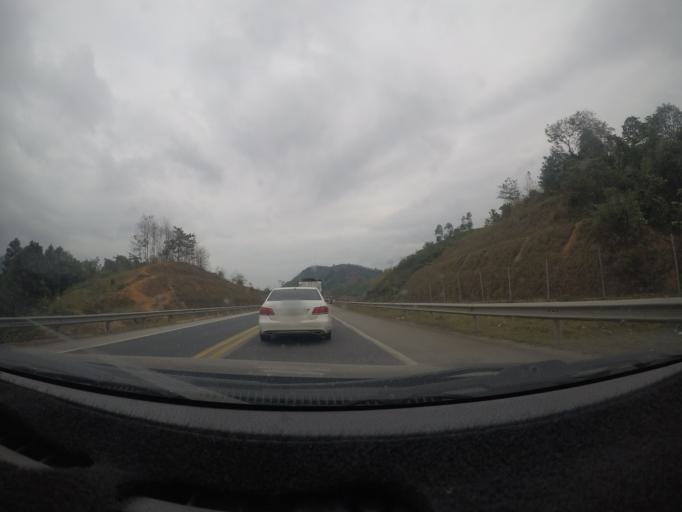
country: VN
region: Lao Cai
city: Thi Tran Pho Rang
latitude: 22.1389
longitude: 104.3842
